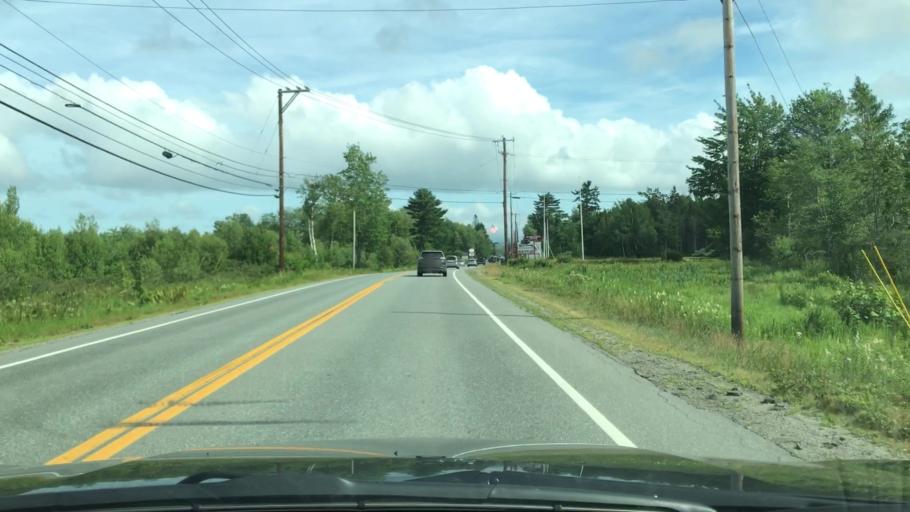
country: US
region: Maine
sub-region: Hancock County
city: Ellsworth
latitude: 44.5014
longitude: -68.3832
